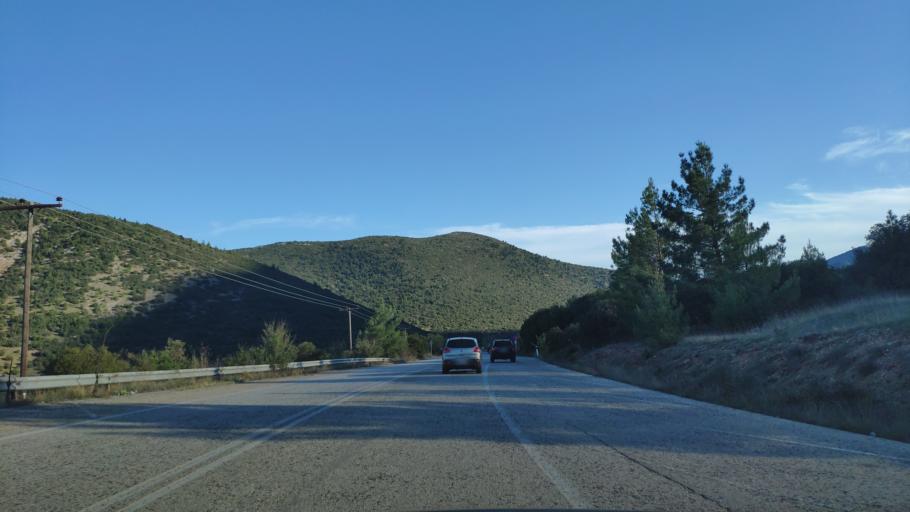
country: GR
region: Peloponnese
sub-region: Nomos Arkadias
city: Tripoli
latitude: 37.6631
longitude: 22.3061
